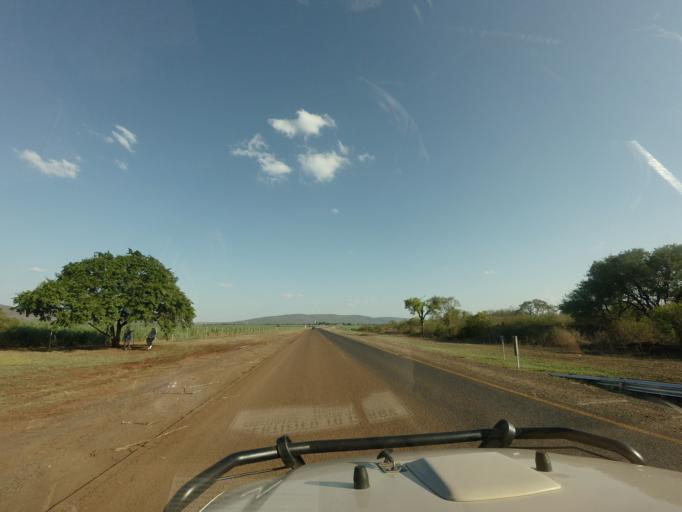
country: ZA
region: Mpumalanga
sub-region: Ehlanzeni District
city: Komatipoort
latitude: -25.4162
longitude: 31.9381
